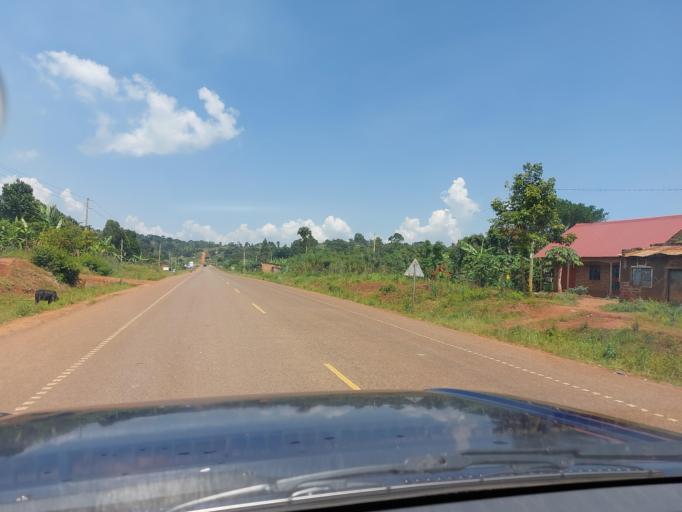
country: UG
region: Central Region
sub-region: Buikwe District
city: Buikwe
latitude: 0.2883
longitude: 33.0851
